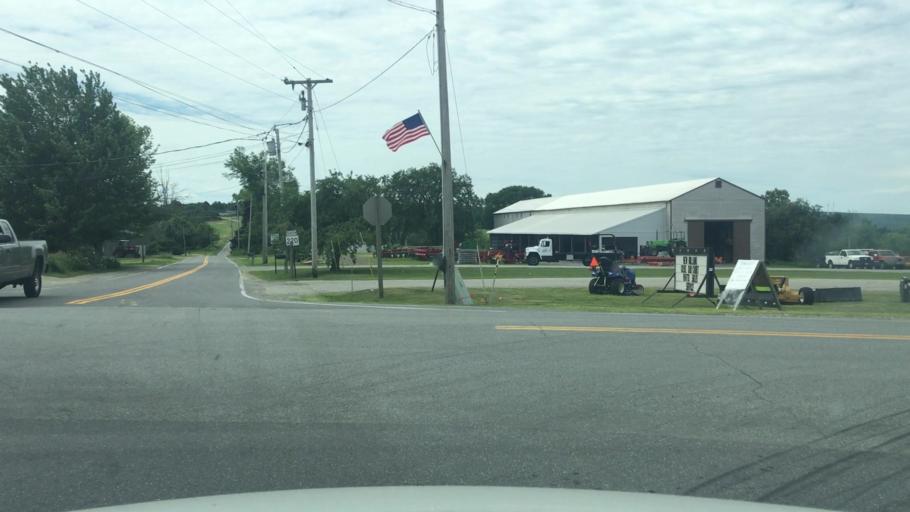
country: US
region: Maine
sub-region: Waldo County
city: Troy
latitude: 44.5327
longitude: -69.2706
